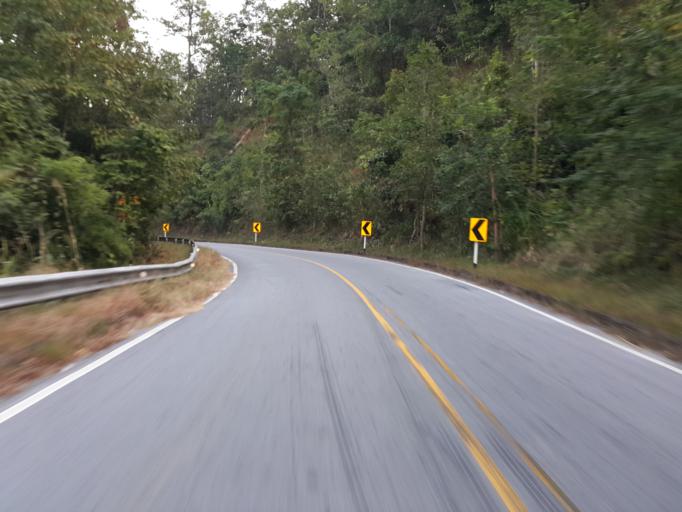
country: TH
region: Lampang
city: Thoen
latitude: 17.6782
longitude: 99.0872
